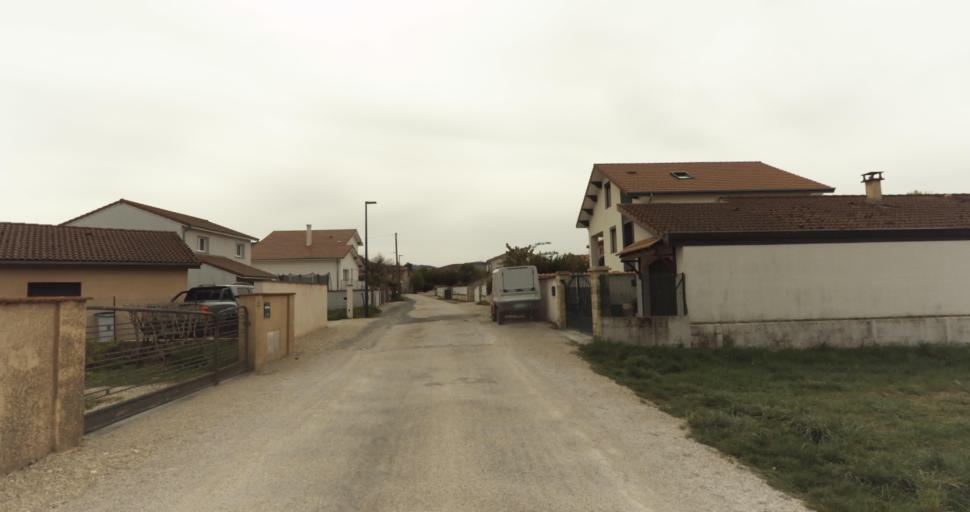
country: FR
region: Rhone-Alpes
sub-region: Departement de l'Ain
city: Amberieu-en-Bugey
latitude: 45.9694
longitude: 5.3546
